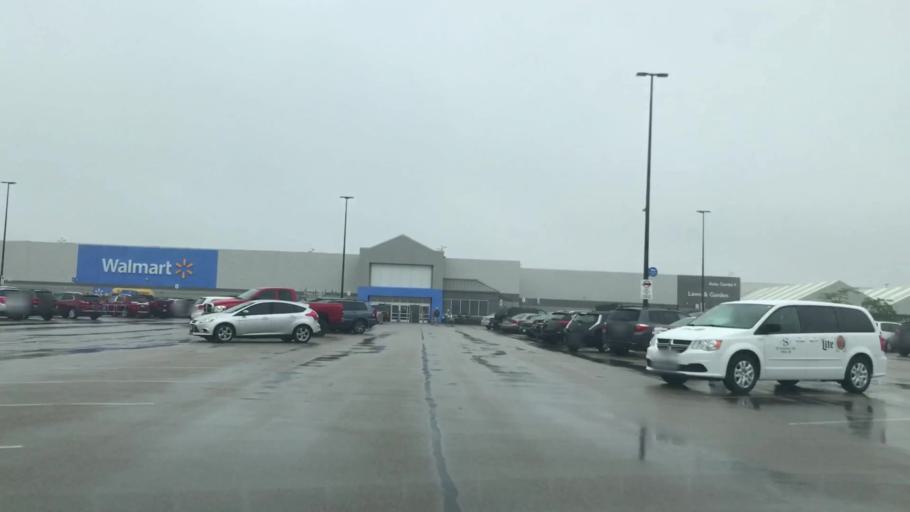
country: US
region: Wisconsin
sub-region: Dodge County
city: Beaver Dam
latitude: 43.4878
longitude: -88.8106
